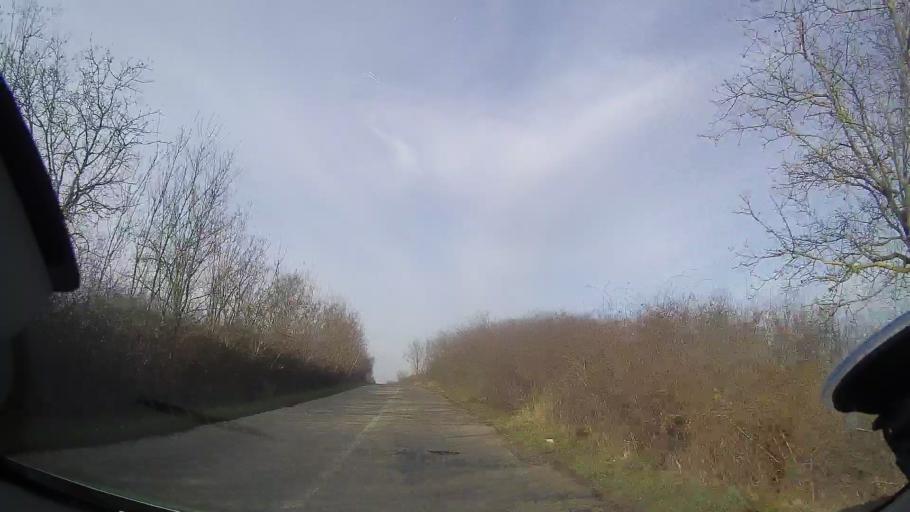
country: RO
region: Bihor
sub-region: Comuna Spinus
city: Spinus
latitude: 47.2122
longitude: 22.1781
